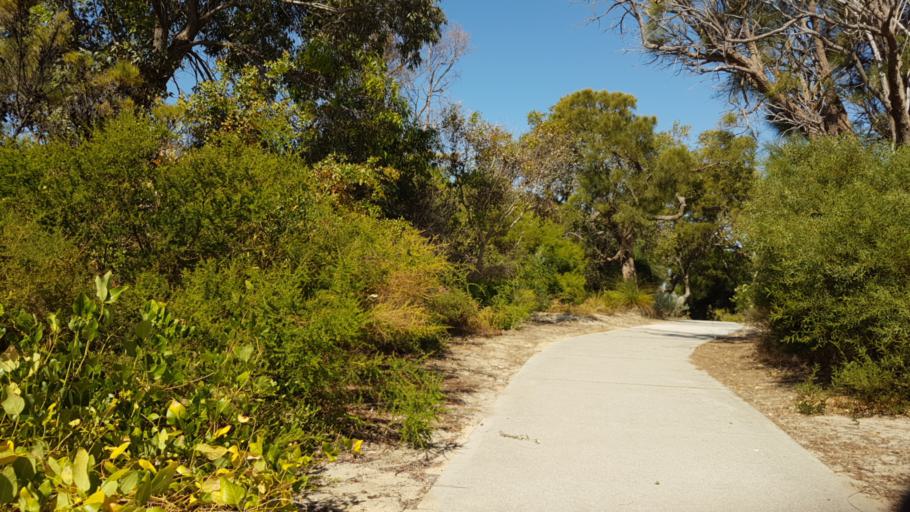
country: AU
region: Western Australia
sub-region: Stirling
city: Karrinyup
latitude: -31.8569
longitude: 115.7723
